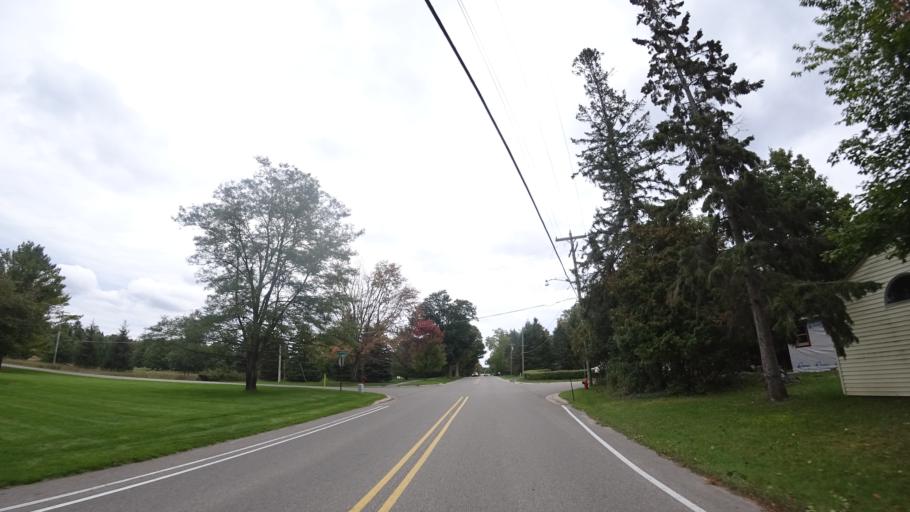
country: US
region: Michigan
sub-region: Emmet County
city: Harbor Springs
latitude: 45.4352
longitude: -85.0016
